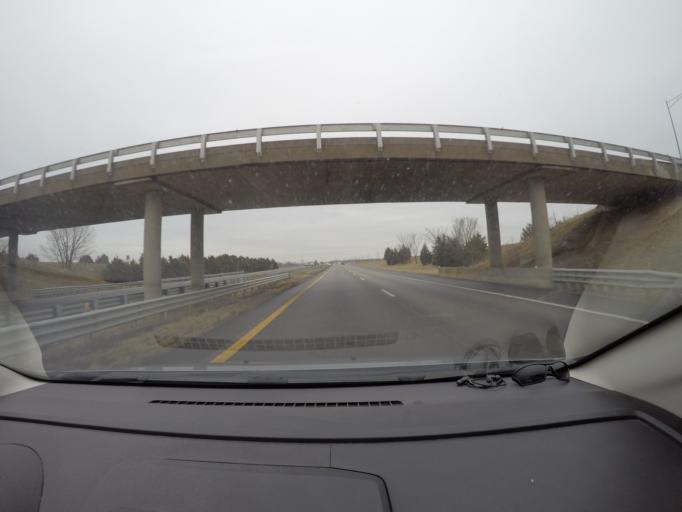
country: US
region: Missouri
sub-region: Warren County
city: Warrenton
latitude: 38.8390
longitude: -91.2247
